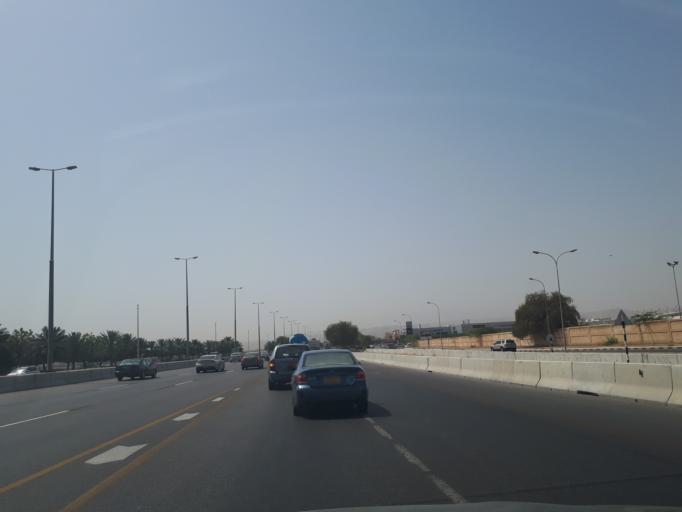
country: OM
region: Muhafazat Masqat
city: As Sib al Jadidah
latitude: 23.6083
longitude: 58.2473
